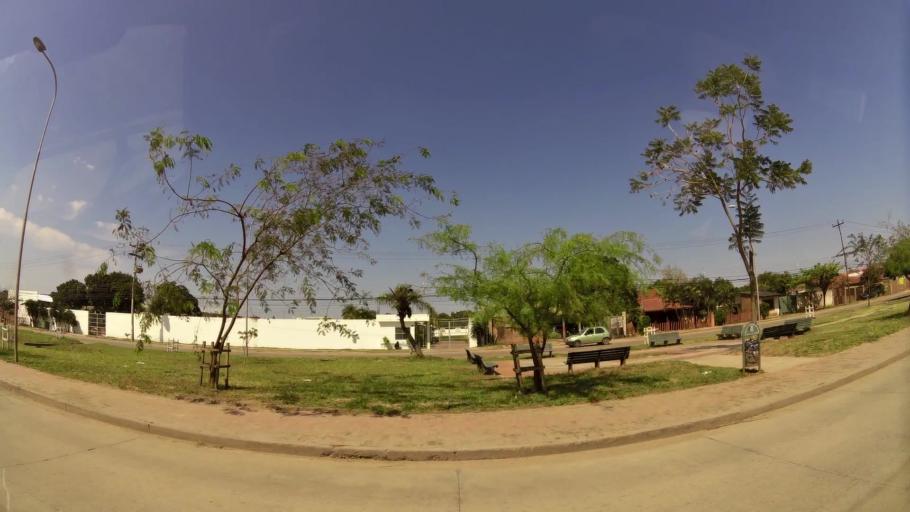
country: BO
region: Santa Cruz
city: Santa Cruz de la Sierra
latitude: -17.7350
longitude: -63.1531
